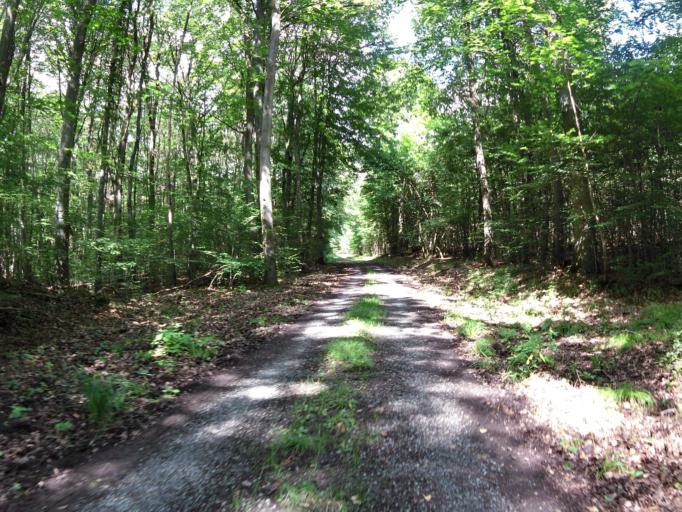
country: DE
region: Bavaria
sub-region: Regierungsbezirk Unterfranken
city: Margetshochheim
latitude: 49.8259
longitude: 9.8367
